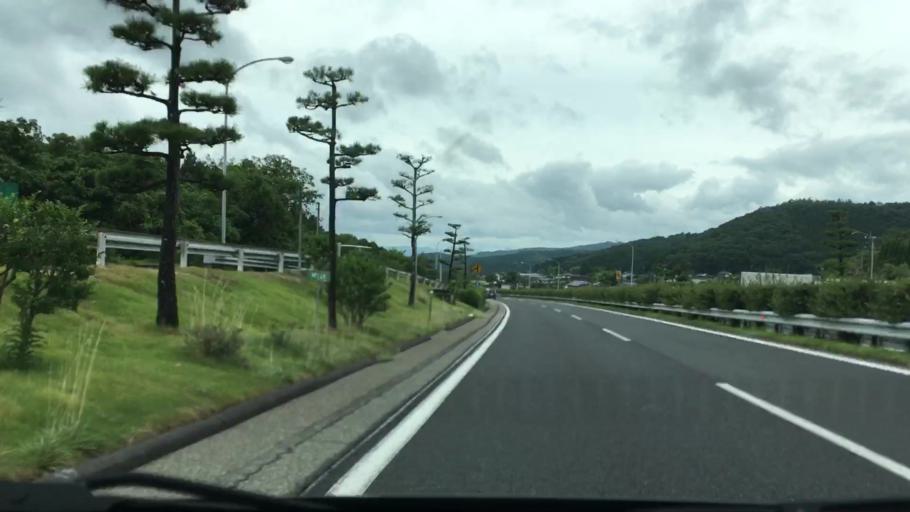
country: JP
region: Okayama
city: Tsuyama
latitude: 35.0217
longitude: 134.1948
